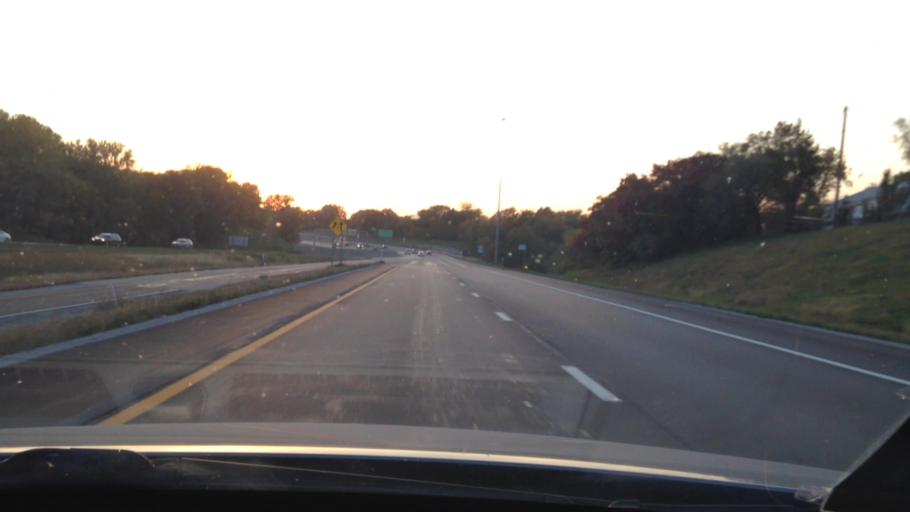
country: US
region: Kansas
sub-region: Wyandotte County
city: Kansas City
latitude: 39.1473
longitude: -94.6604
